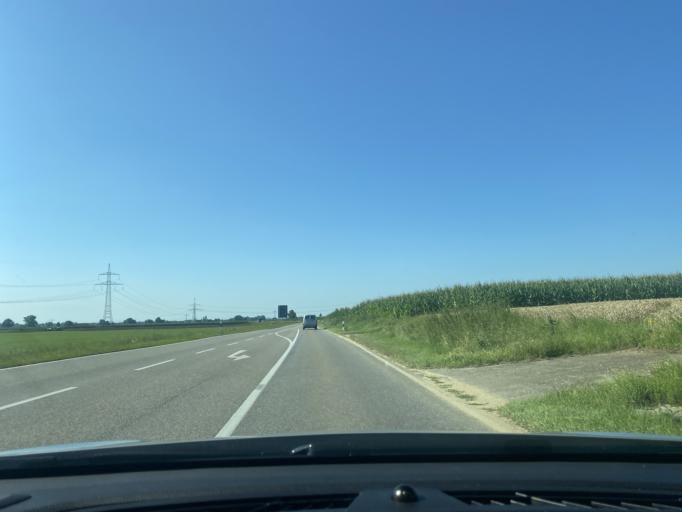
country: DE
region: Bavaria
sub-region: Upper Bavaria
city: Eitting
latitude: 48.3511
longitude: 11.8981
